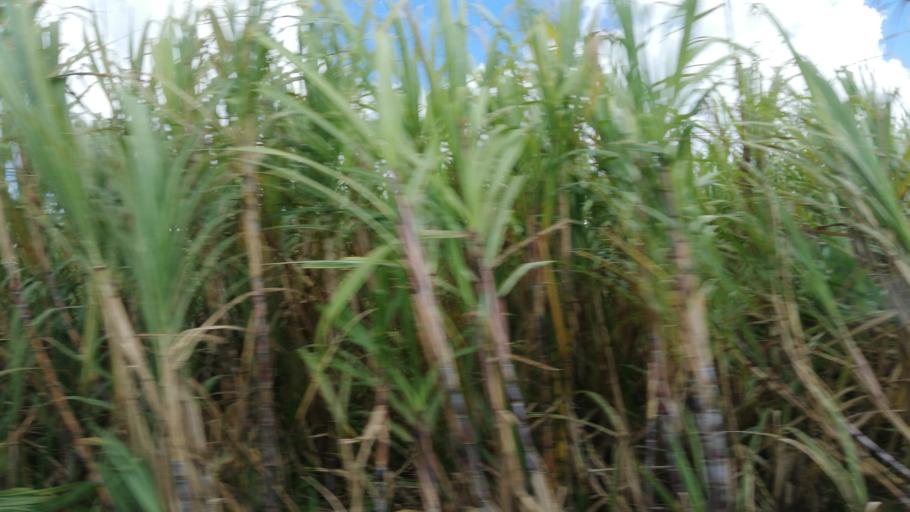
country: MU
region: Flacq
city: Saint Julien
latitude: -20.2399
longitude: 57.6386
